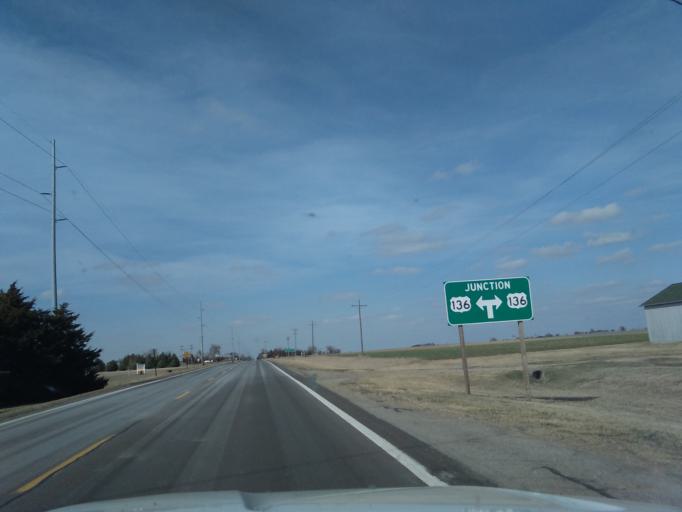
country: US
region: Nebraska
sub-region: Gage County
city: Beatrice
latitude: 40.2069
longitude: -96.9353
